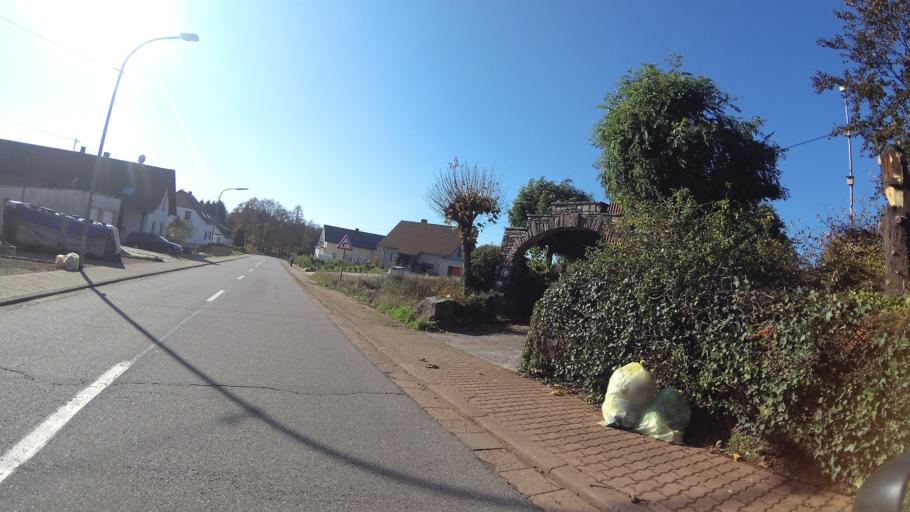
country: DE
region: Saarland
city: Losheim
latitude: 49.5446
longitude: 6.7292
